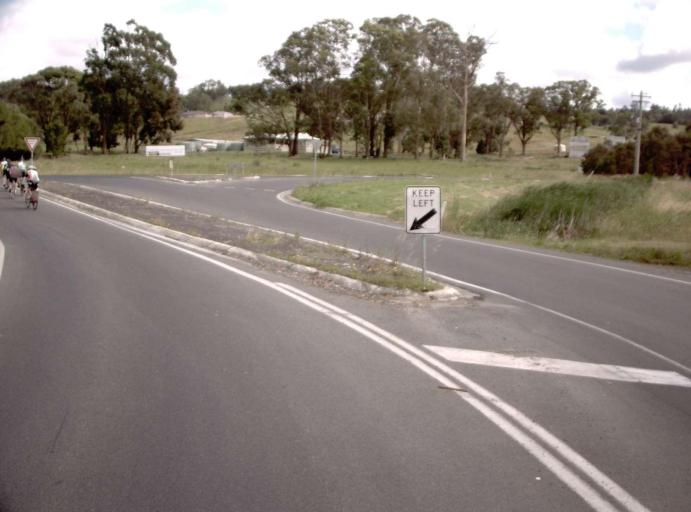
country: AU
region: Victoria
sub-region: Latrobe
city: Morwell
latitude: -38.1618
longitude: 146.4071
